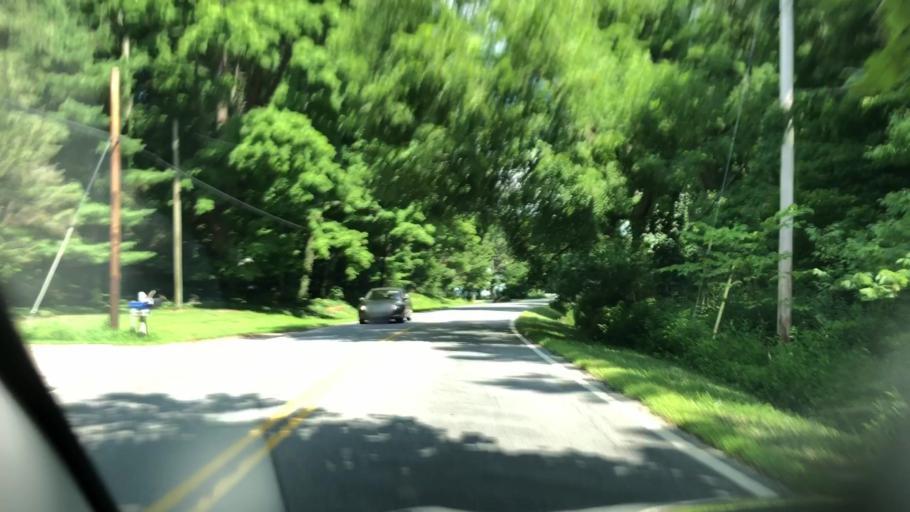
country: US
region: Ohio
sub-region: Summit County
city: Montrose-Ghent
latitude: 41.1606
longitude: -81.6488
